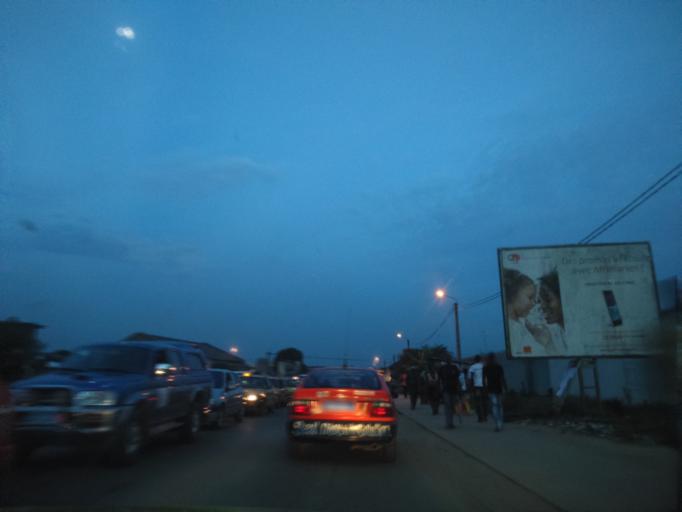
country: CI
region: Lagunes
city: Abobo
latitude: 5.4092
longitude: -3.9930
